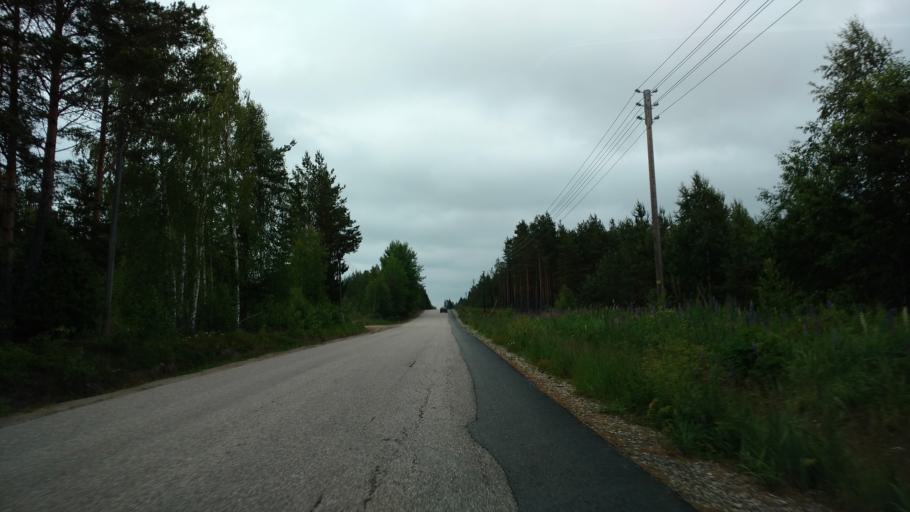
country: FI
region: Varsinais-Suomi
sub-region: Salo
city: Kiikala
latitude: 60.4365
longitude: 23.6102
